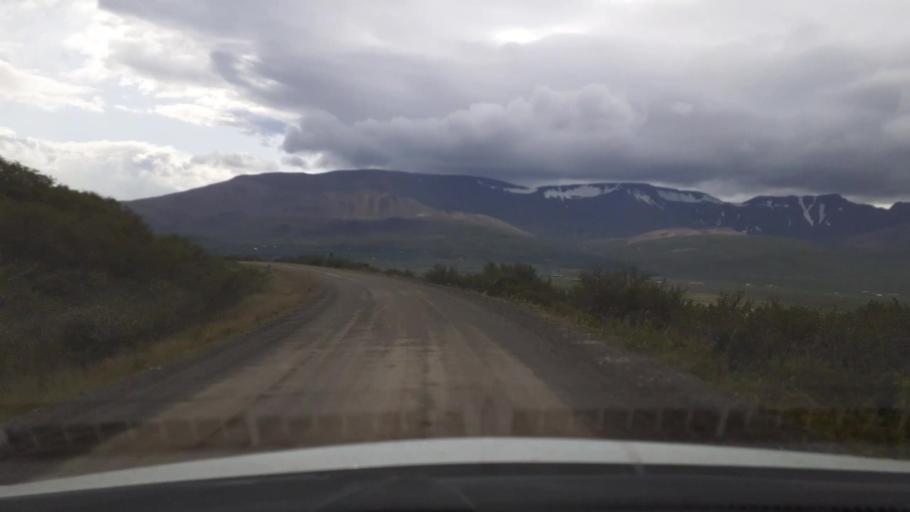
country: IS
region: West
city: Borgarnes
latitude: 64.5532
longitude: -21.6239
